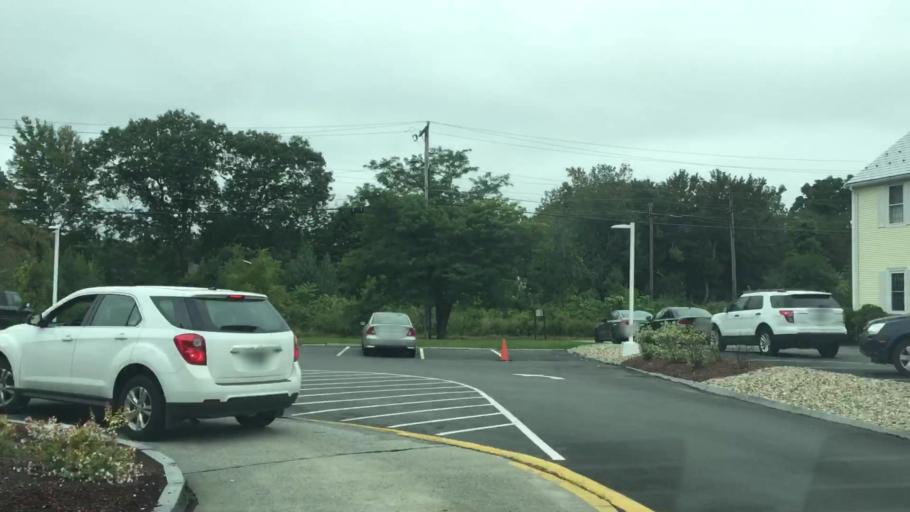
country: US
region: Massachusetts
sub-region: Essex County
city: North Andover
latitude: 42.7002
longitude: -71.1188
